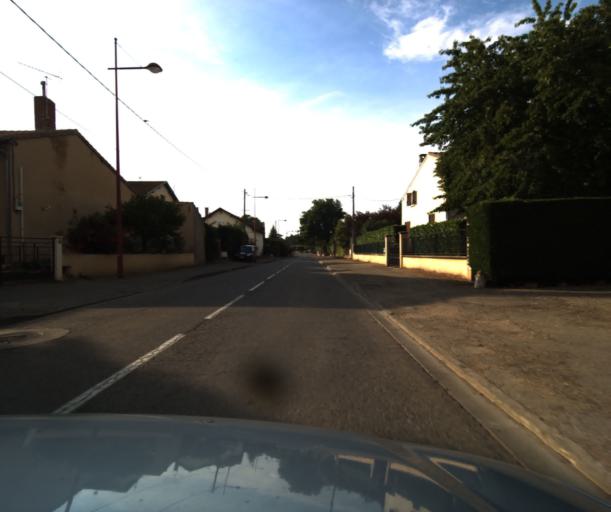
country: FR
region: Midi-Pyrenees
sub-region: Departement du Tarn-et-Garonne
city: Castelsarrasin
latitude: 44.0334
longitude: 1.1067
